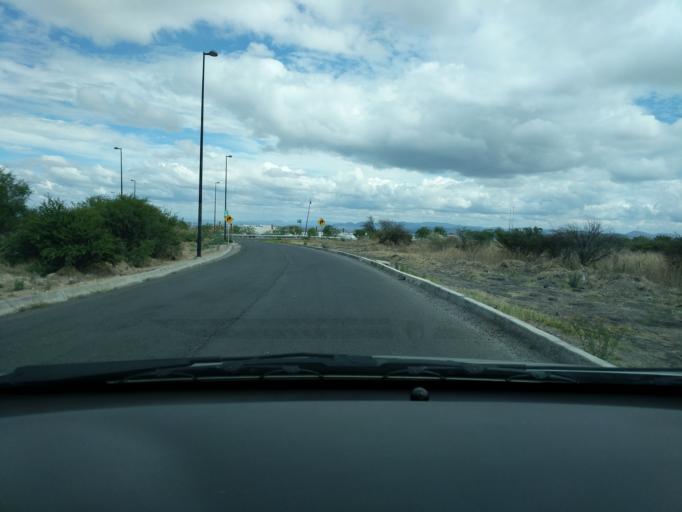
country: MX
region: Queretaro
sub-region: El Marques
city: La Pradera
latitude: 20.6661
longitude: -100.3158
